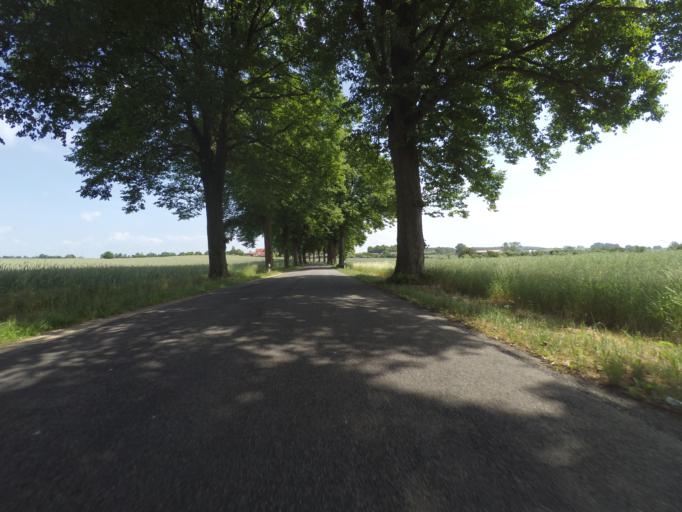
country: DE
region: Mecklenburg-Vorpommern
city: Lubz
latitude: 53.4439
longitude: 12.0773
